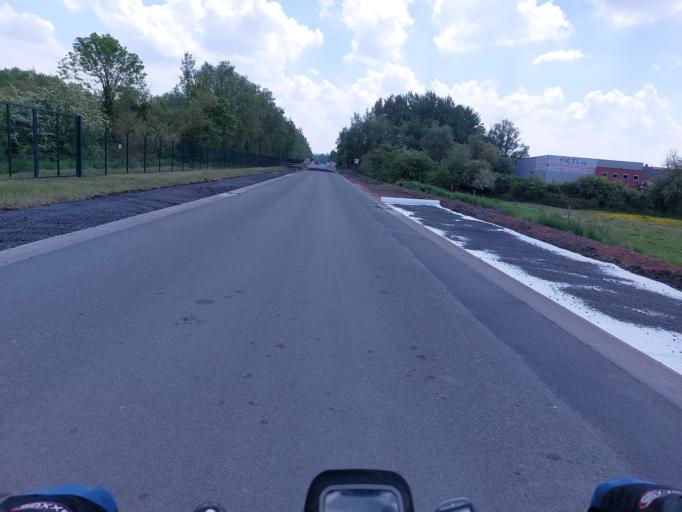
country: BE
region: Wallonia
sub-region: Province du Hainaut
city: Quaregnon
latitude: 50.4705
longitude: 3.8568
